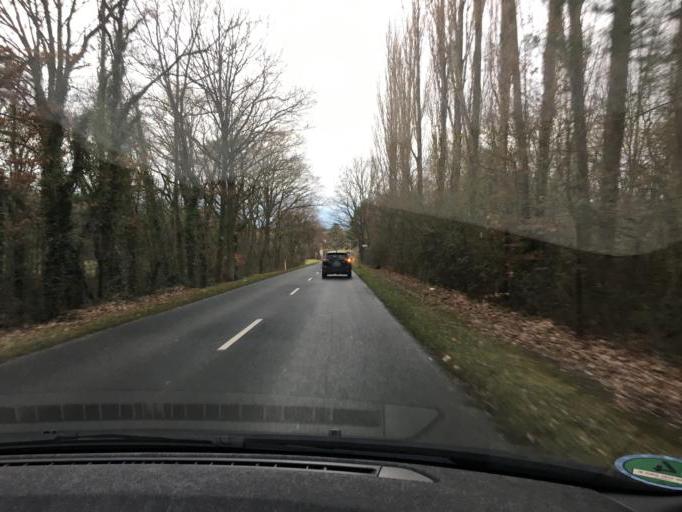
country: DE
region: North Rhine-Westphalia
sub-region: Regierungsbezirk Koln
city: Mechernich
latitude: 50.6245
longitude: 6.6971
